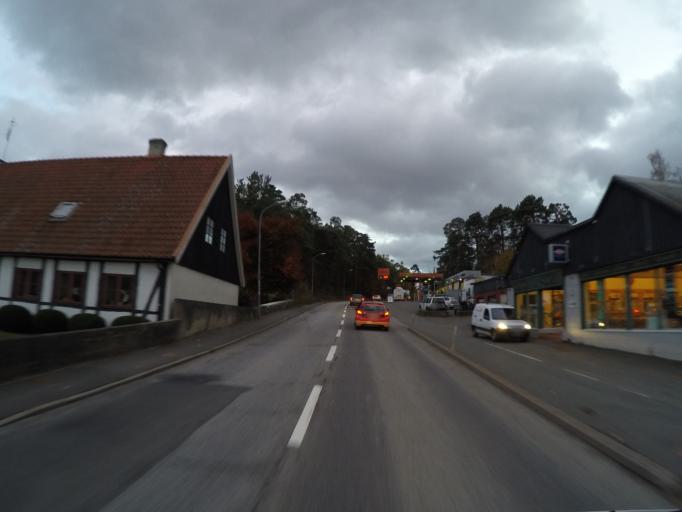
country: SE
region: Skane
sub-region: Kristianstads Kommun
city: Degeberga
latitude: 55.8350
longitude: 14.0903
